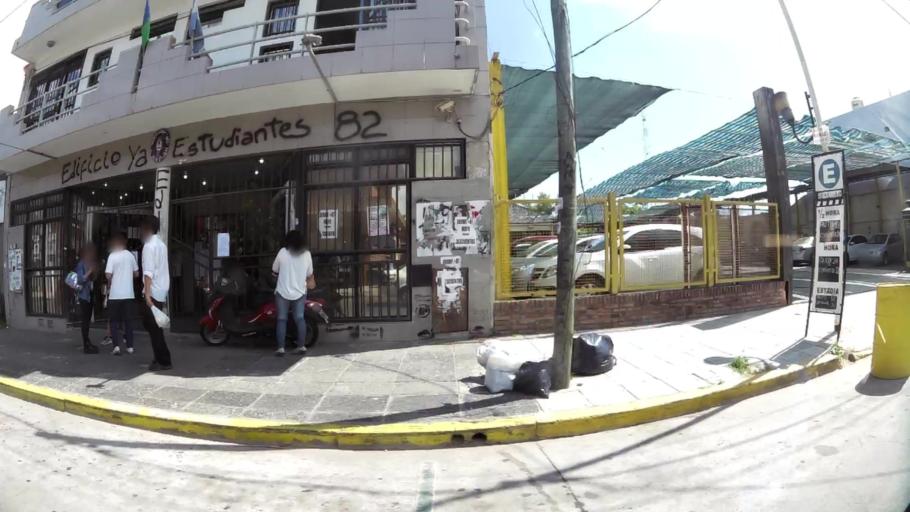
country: AR
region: Buenos Aires
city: San Justo
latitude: -34.6804
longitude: -58.5599
